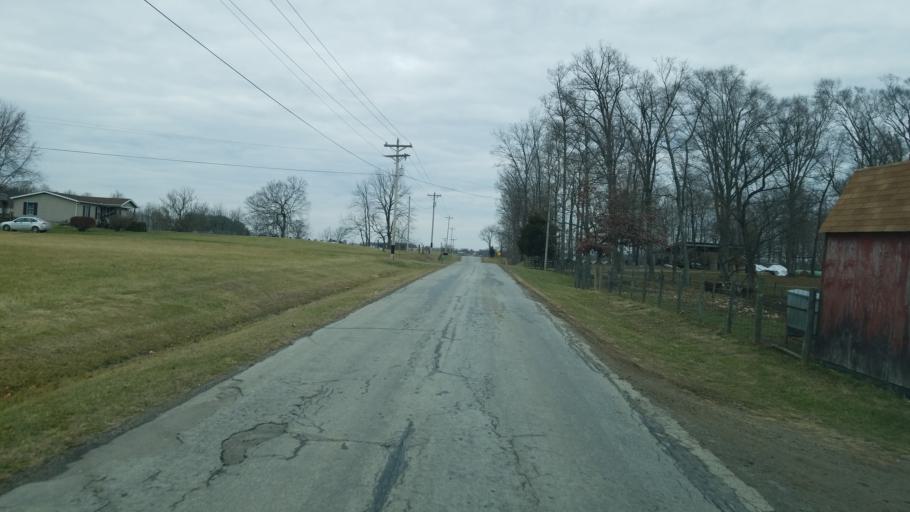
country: US
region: Ohio
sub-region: Highland County
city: Hillsboro
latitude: 39.2177
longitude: -83.4858
